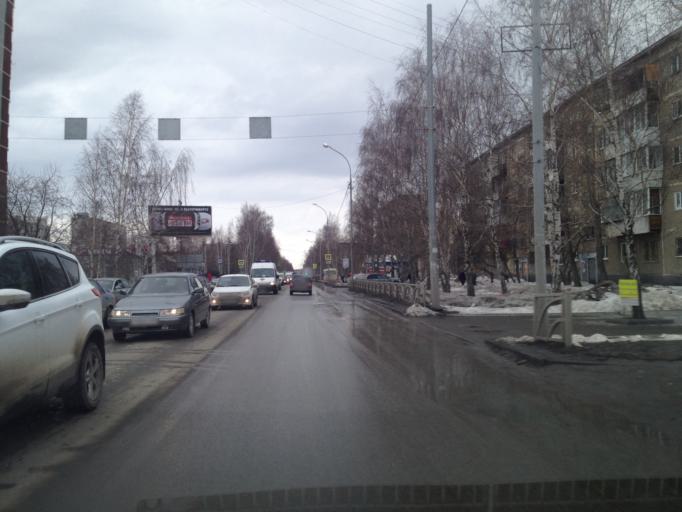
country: RU
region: Sverdlovsk
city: Sovkhoznyy
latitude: 56.8097
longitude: 60.5473
